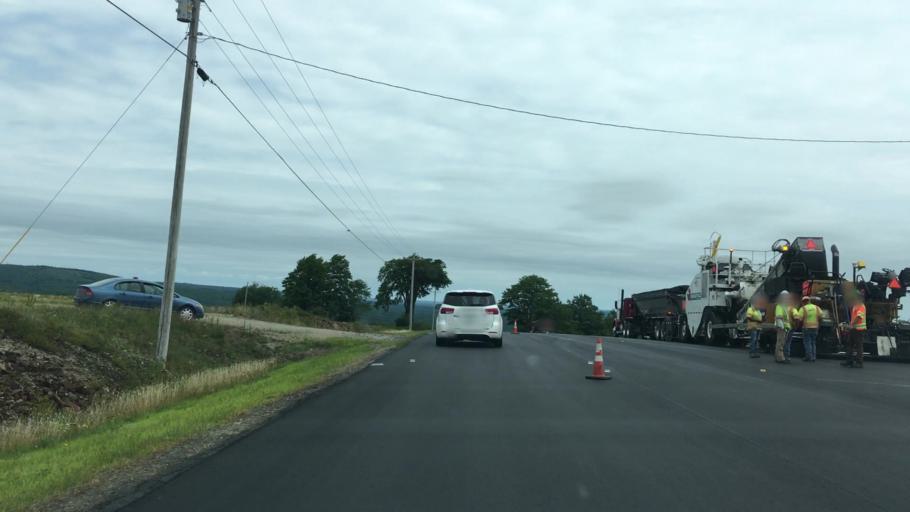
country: US
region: Maine
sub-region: Washington County
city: Machias
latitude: 44.9672
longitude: -67.6487
